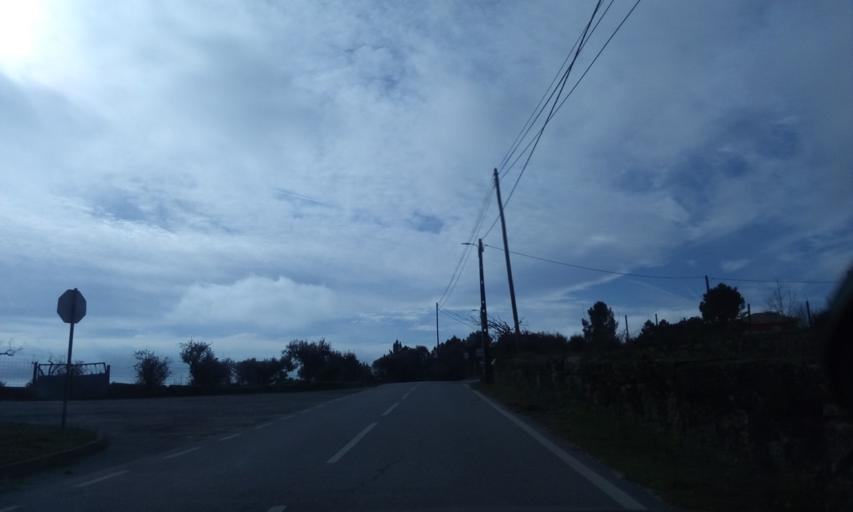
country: PT
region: Guarda
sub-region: Aguiar da Beira
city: Aguiar da Beira
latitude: 40.7579
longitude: -7.5428
